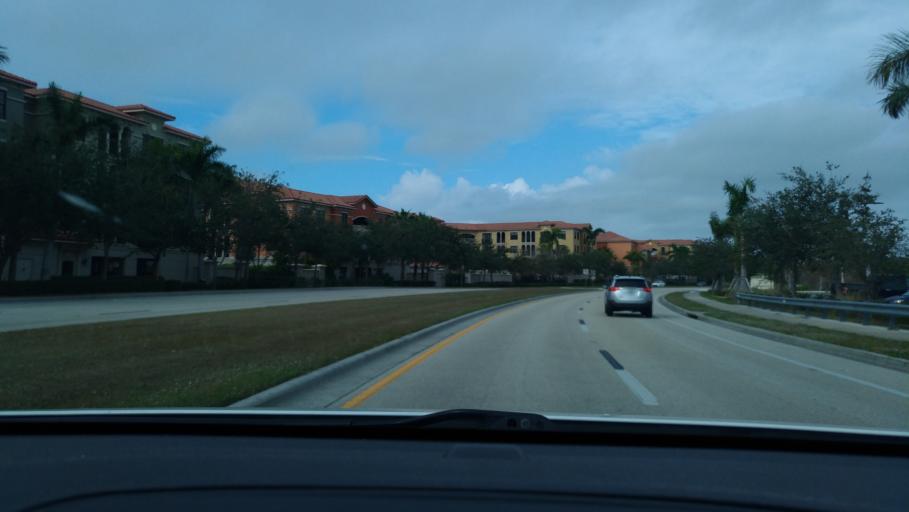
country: US
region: Florida
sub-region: Lee County
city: Estero
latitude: 26.3998
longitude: -81.8059
